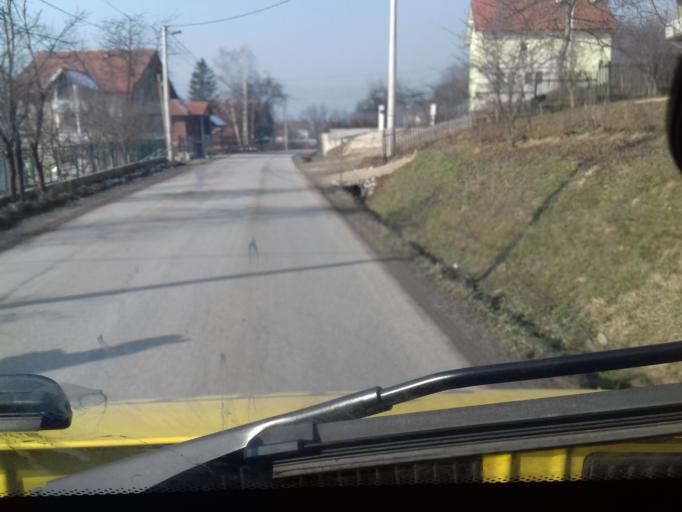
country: BA
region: Federation of Bosnia and Herzegovina
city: Ilijas
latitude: 43.9424
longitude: 18.2744
